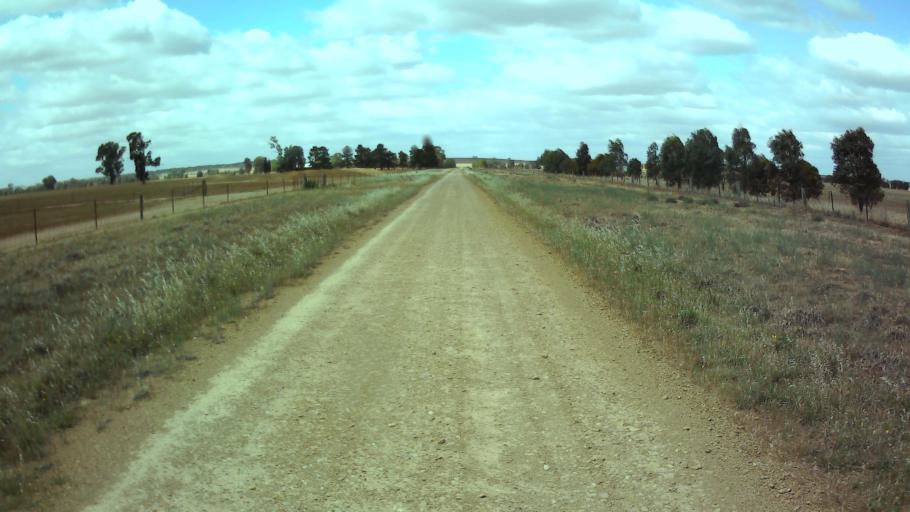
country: AU
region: New South Wales
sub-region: Weddin
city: Grenfell
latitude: -34.0554
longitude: 148.3312
